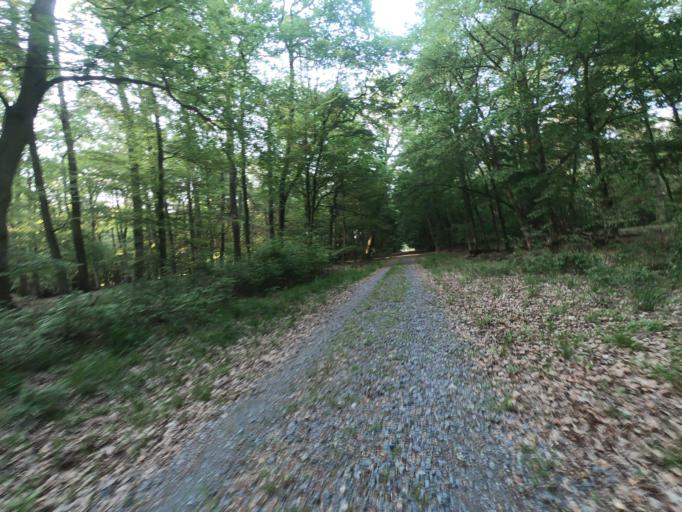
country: DE
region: Hesse
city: Morfelden-Walldorf
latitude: 49.9896
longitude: 8.5510
